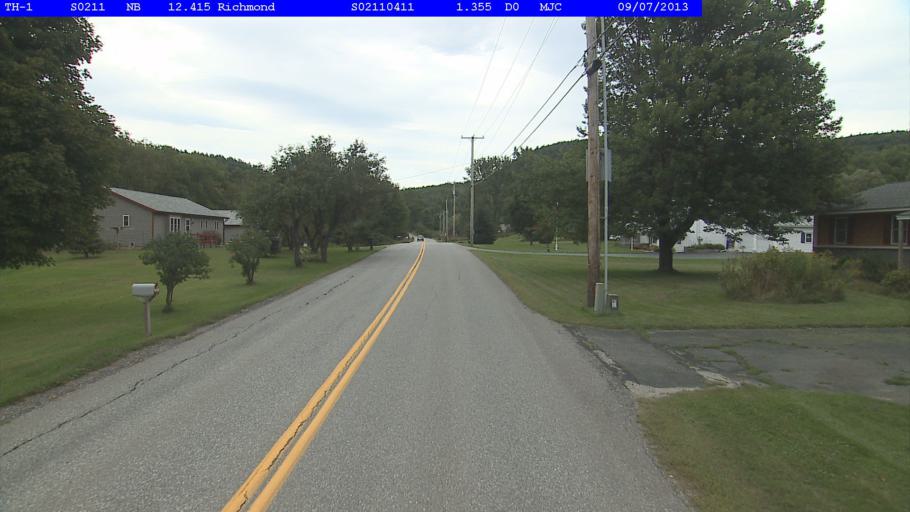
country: US
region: Vermont
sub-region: Chittenden County
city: Williston
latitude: 44.3710
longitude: -72.9997
